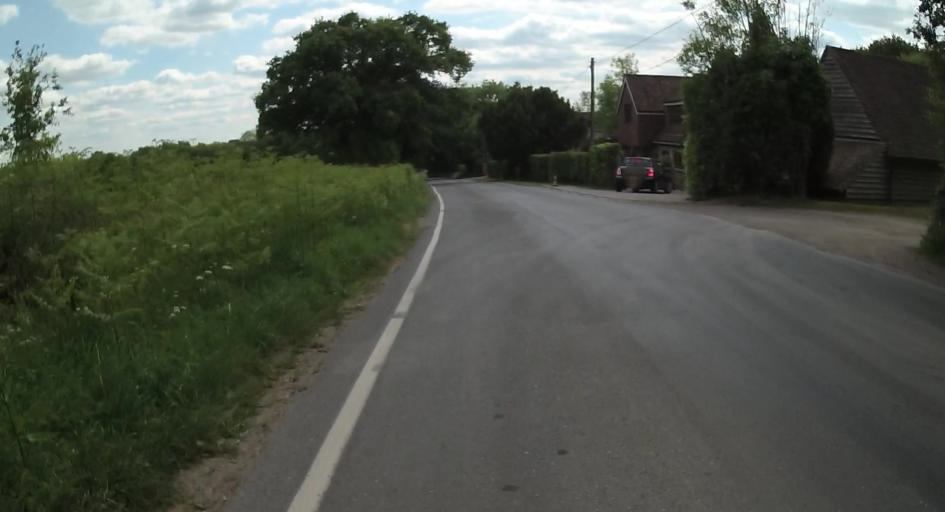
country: GB
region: England
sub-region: Surrey
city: Farnham
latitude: 51.2286
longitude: -0.8363
